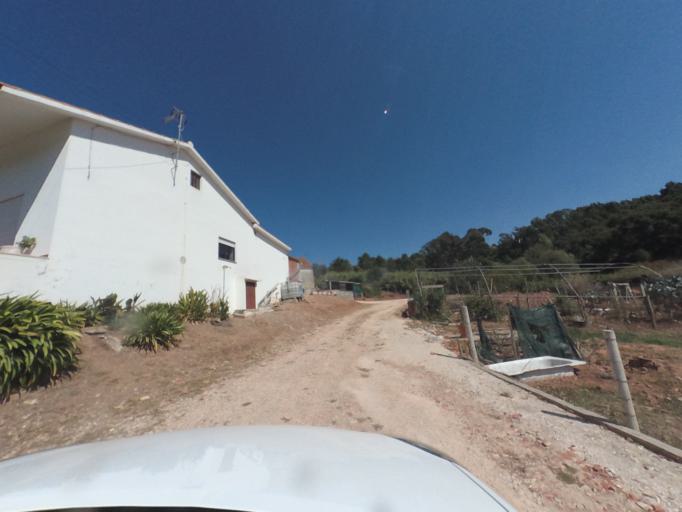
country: PT
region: Leiria
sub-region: Alcobaca
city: Turquel
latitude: 39.4846
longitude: -8.9933
